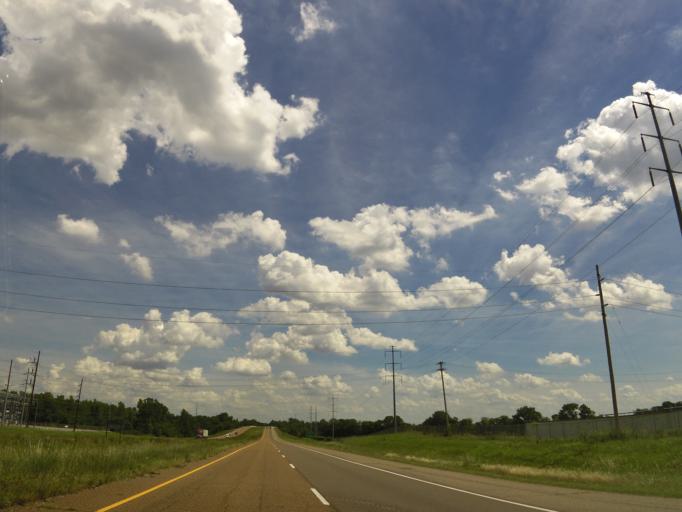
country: US
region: Tennessee
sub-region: Dyer County
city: Dyersburg
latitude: 36.0588
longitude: -89.3394
